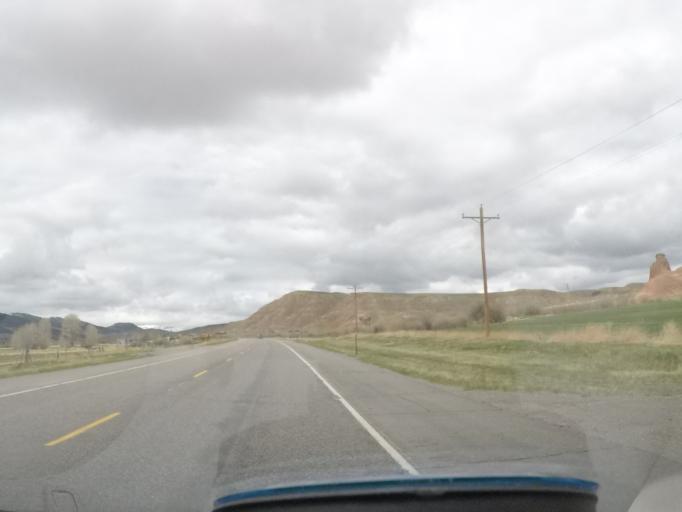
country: US
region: Wyoming
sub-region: Sublette County
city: Pinedale
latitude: 43.5647
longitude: -109.7028
